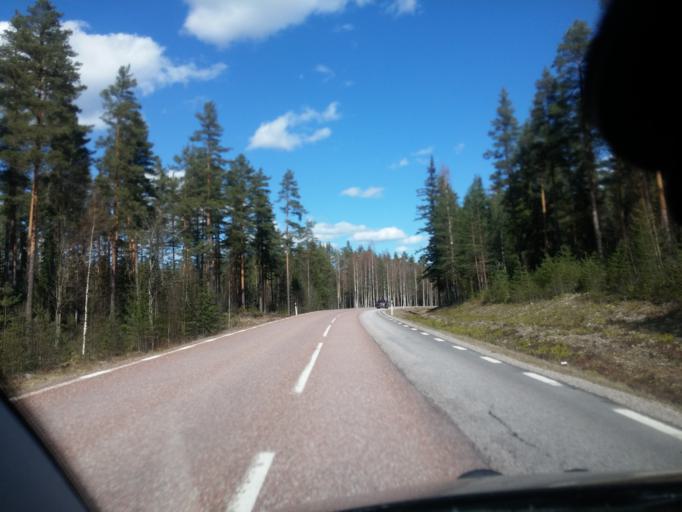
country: SE
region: Dalarna
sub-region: Faluns Kommun
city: Falun
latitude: 60.6936
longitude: 15.7274
